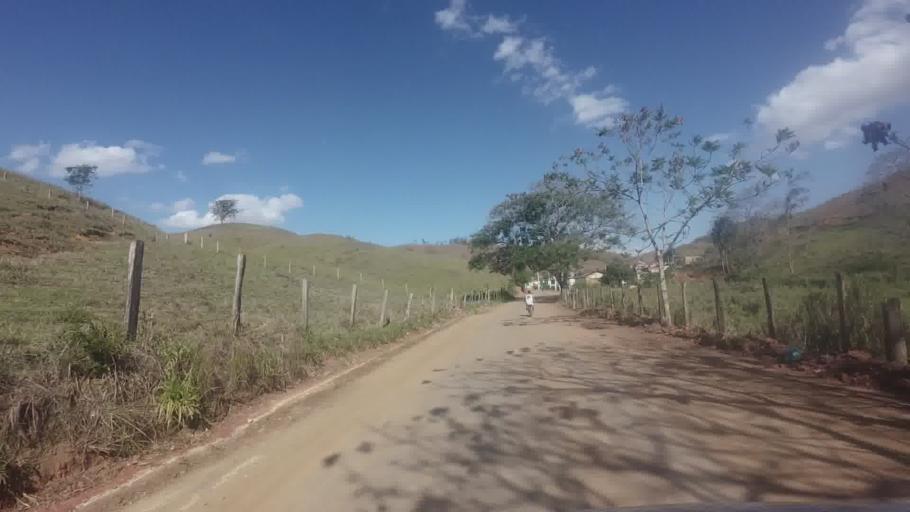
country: BR
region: Rio de Janeiro
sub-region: Bom Jesus Do Itabapoana
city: Bom Jesus do Itabapoana
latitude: -21.1206
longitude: -41.6608
